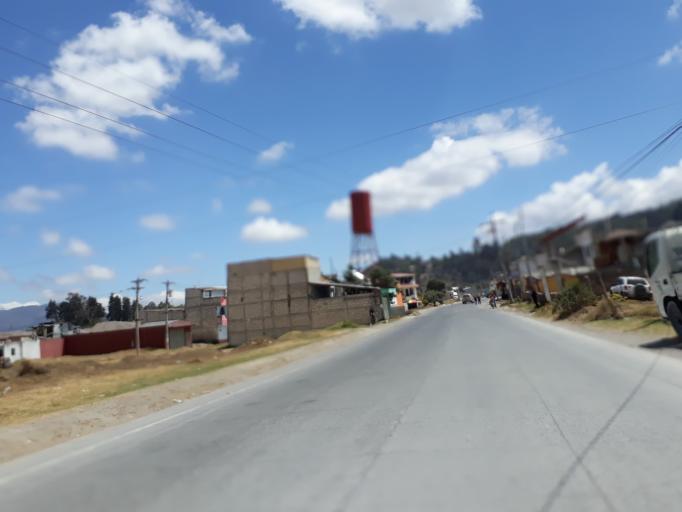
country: GT
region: Quetzaltenango
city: Quetzaltenango
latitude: 14.8167
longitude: -91.5448
